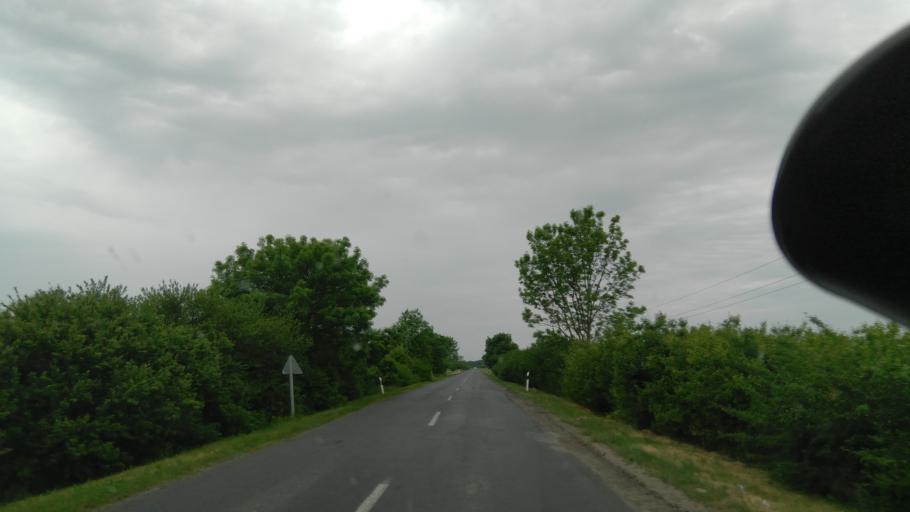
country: HU
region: Bekes
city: Doboz
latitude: 46.7257
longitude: 21.2924
